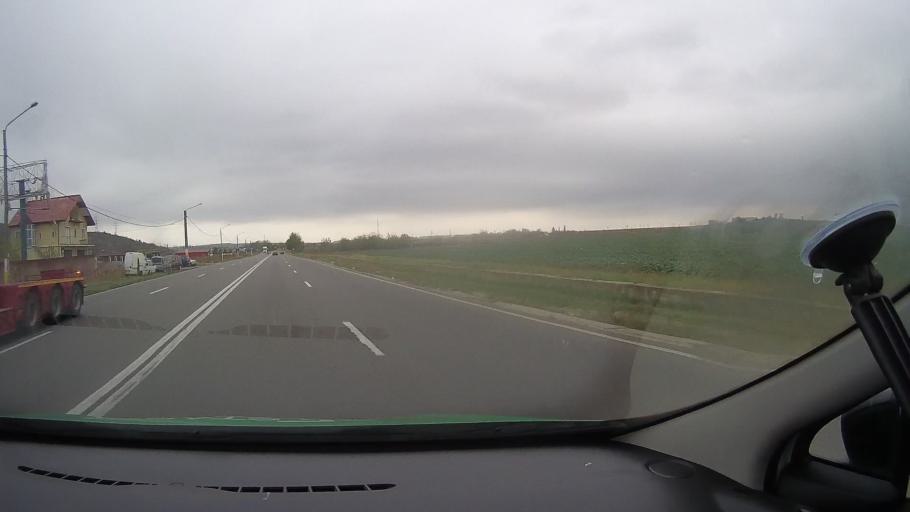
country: RO
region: Constanta
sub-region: Oras Murfatlar
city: Murfatlar
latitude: 44.1703
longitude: 28.4345
